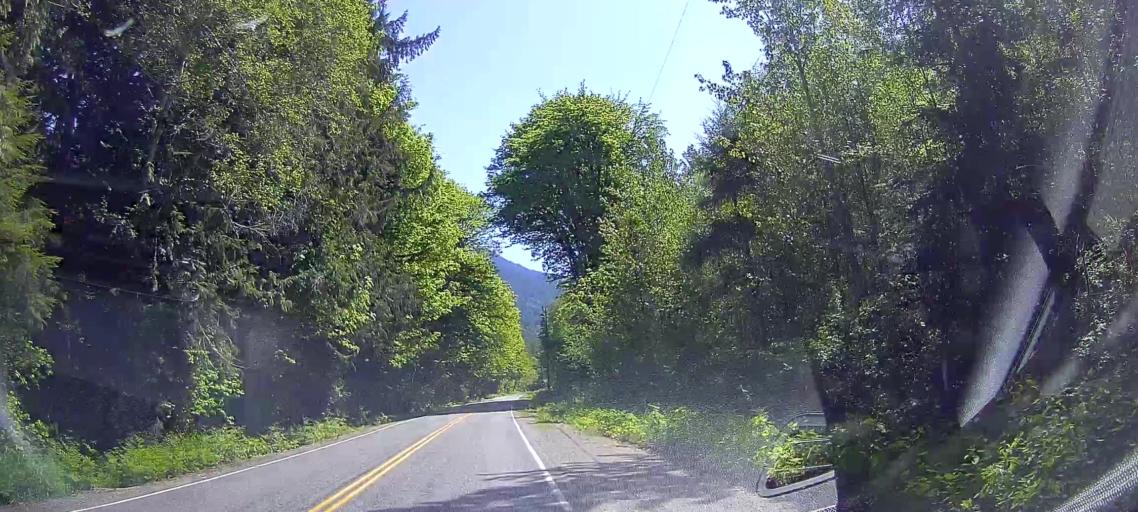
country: US
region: Washington
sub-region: Snohomish County
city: Darrington
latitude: 48.5099
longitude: -121.6780
